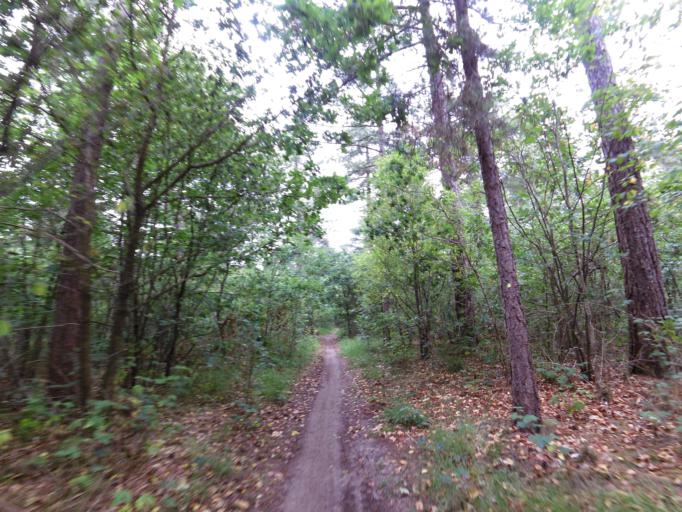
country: NL
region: North Brabant
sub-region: Gemeente Breda
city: Hoge Vucht
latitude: 51.6358
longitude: 4.8166
